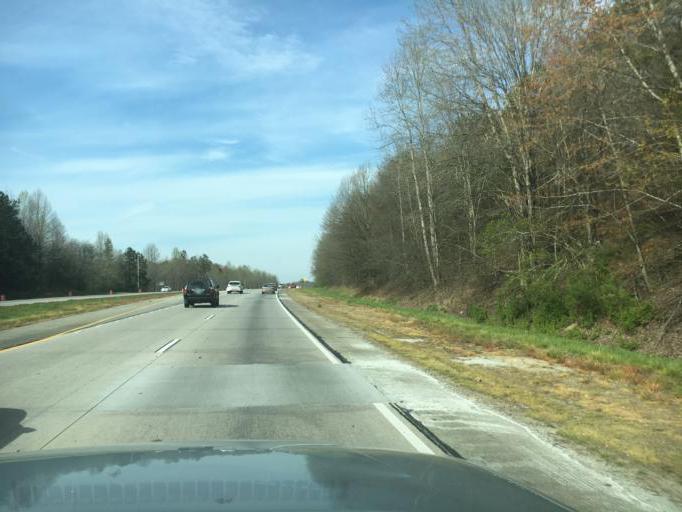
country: US
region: Georgia
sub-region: Hall County
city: Gainesville
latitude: 34.3258
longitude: -83.7861
